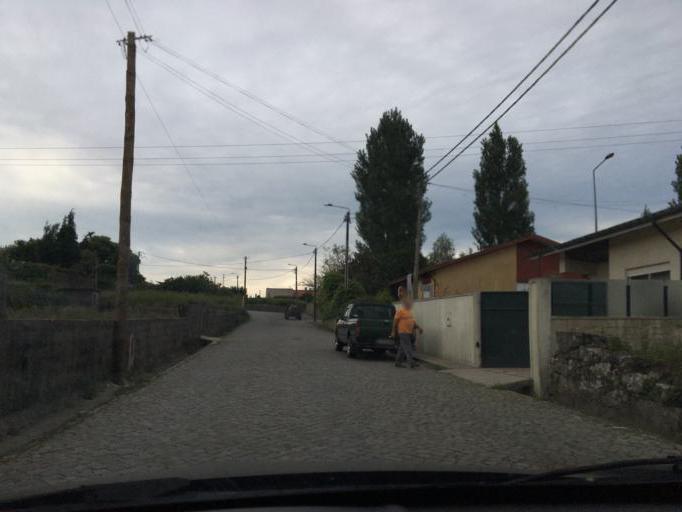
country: PT
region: Porto
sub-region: Maia
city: Anta
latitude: 41.2839
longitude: -8.6112
